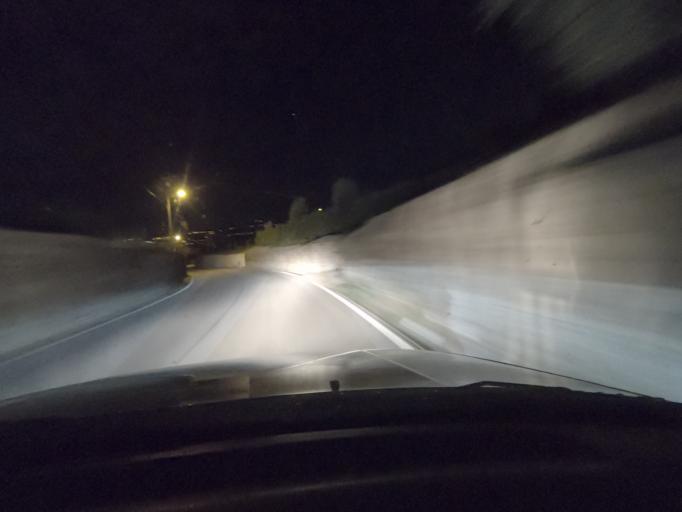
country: PT
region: Vila Real
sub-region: Peso da Regua
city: Godim
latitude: 41.1868
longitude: -7.7930
